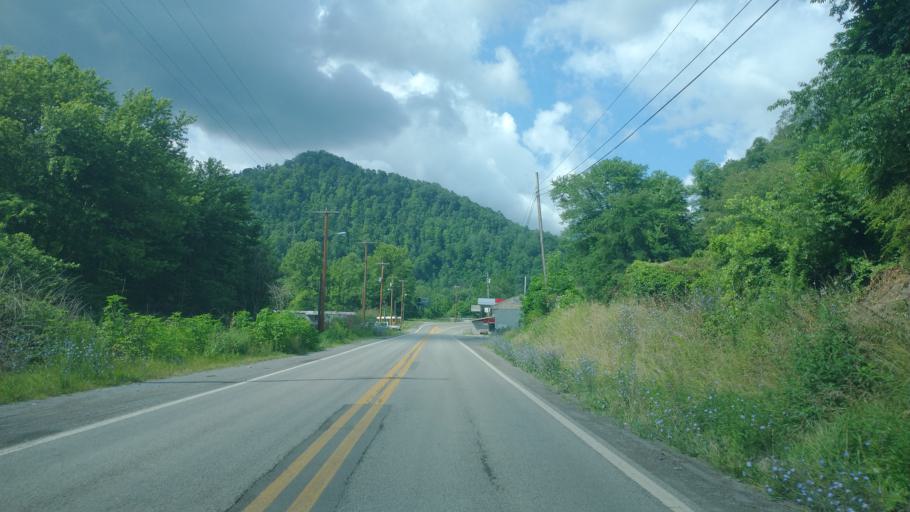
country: US
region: West Virginia
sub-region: McDowell County
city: Welch
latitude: 37.4159
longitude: -81.5201
